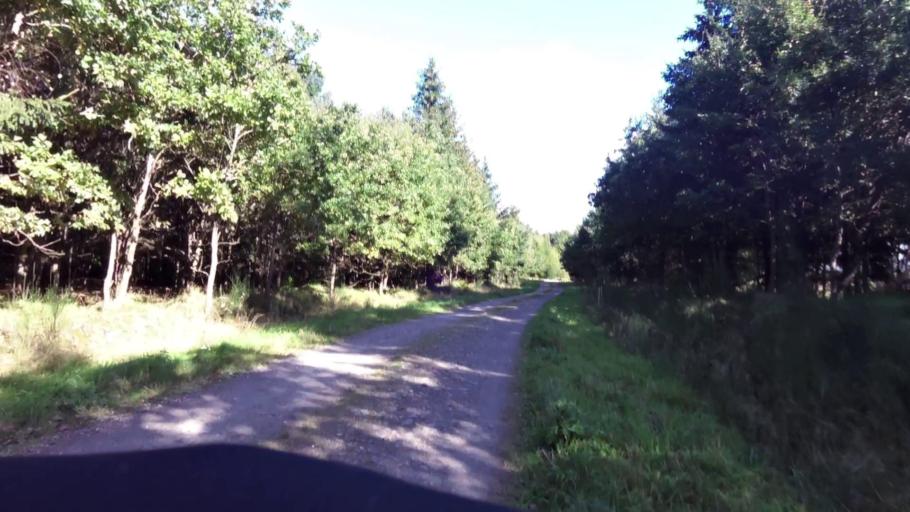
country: PL
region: West Pomeranian Voivodeship
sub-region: Powiat bialogardzki
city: Bialogard
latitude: 53.9960
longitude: 16.1212
